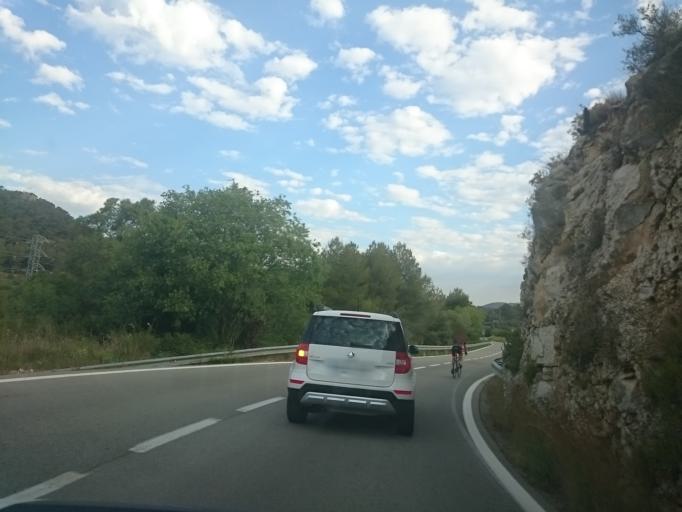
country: ES
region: Catalonia
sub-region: Provincia de Barcelona
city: Cubelles
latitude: 41.2332
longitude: 1.6649
